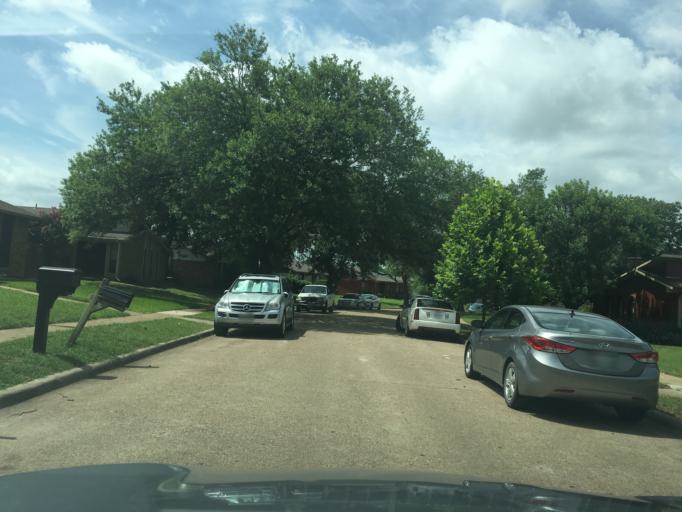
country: US
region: Texas
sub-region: Dallas County
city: Richardson
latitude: 32.9136
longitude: -96.7062
